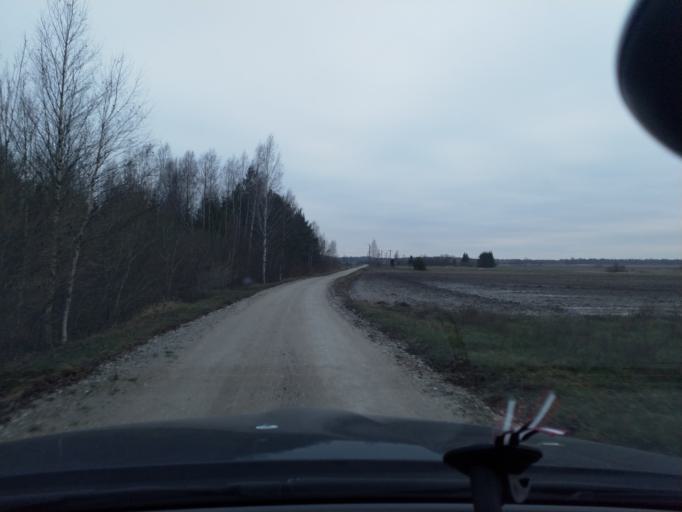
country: LV
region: Rucavas
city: Rucava
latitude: 56.2452
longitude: 21.2527
